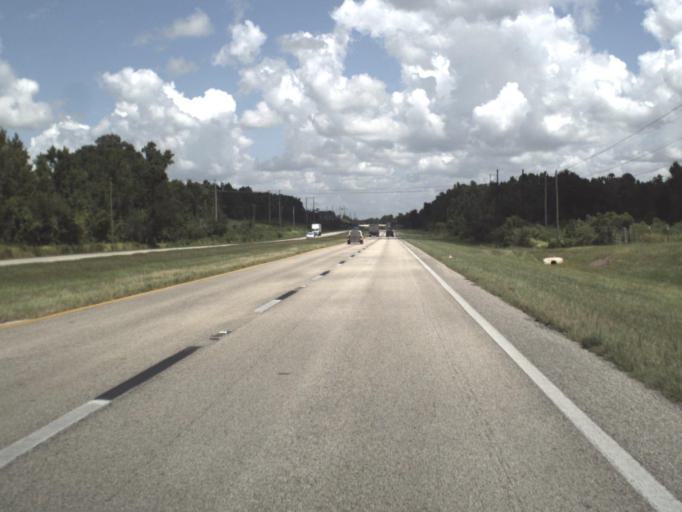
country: US
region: Florida
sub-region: Polk County
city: Fort Meade
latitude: 27.7116
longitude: -81.8056
